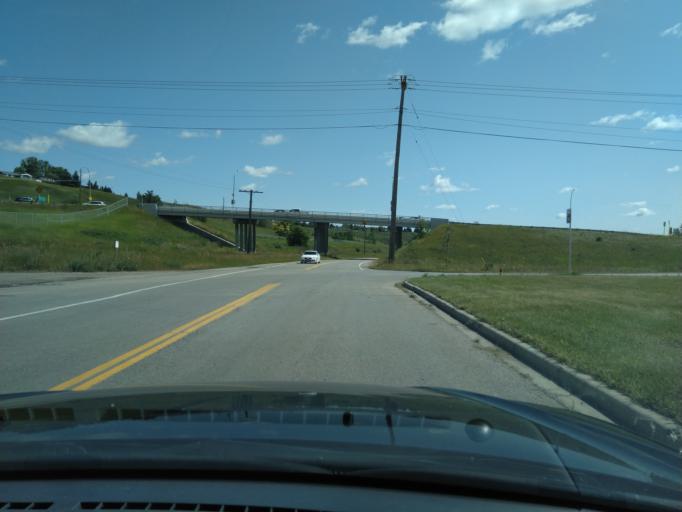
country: CA
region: Alberta
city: Calgary
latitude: 51.1012
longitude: -114.2115
